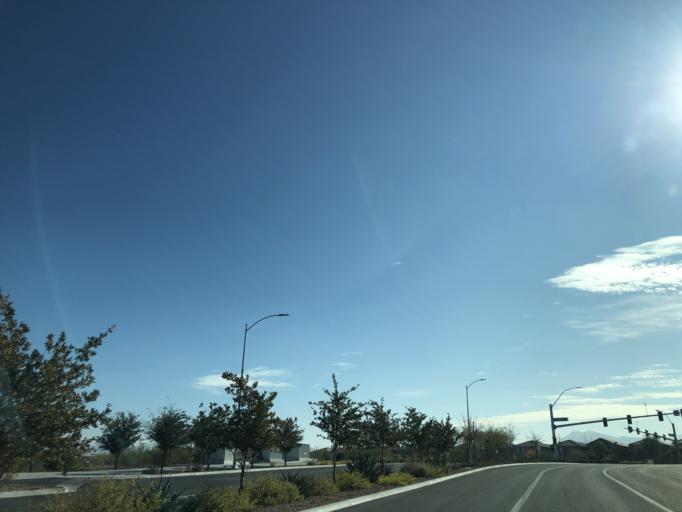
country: US
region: Nevada
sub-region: Clark County
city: Whitney
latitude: 36.0725
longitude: -115.0328
